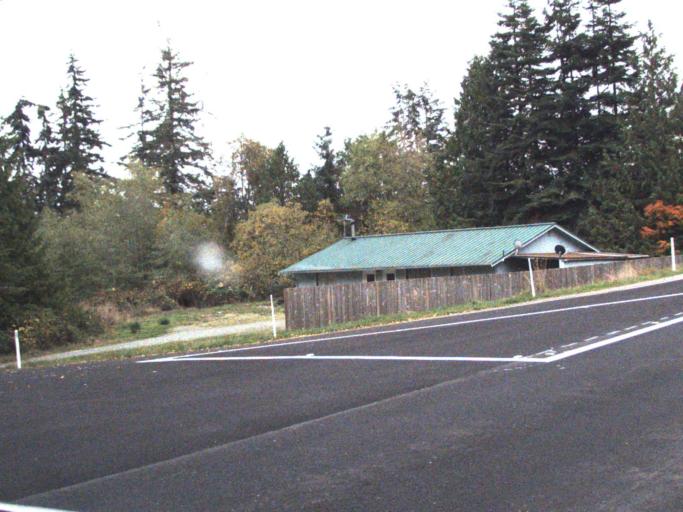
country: US
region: Washington
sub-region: Island County
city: Freeland
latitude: 48.0893
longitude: -122.5686
